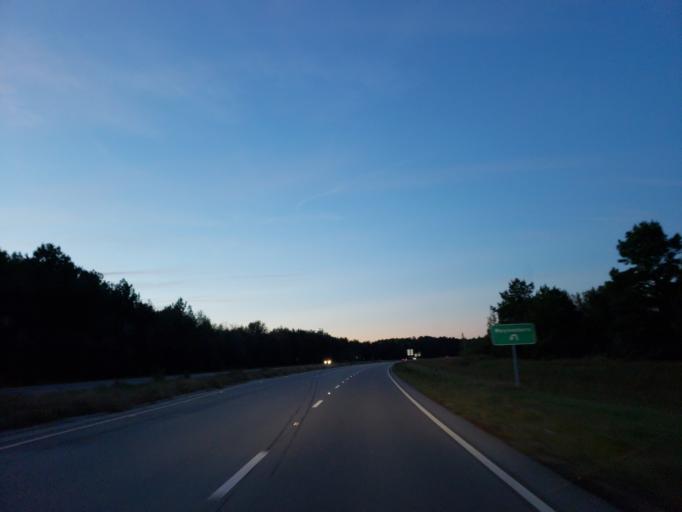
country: US
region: Mississippi
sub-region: Clarke County
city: Quitman
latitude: 31.8513
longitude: -88.7180
